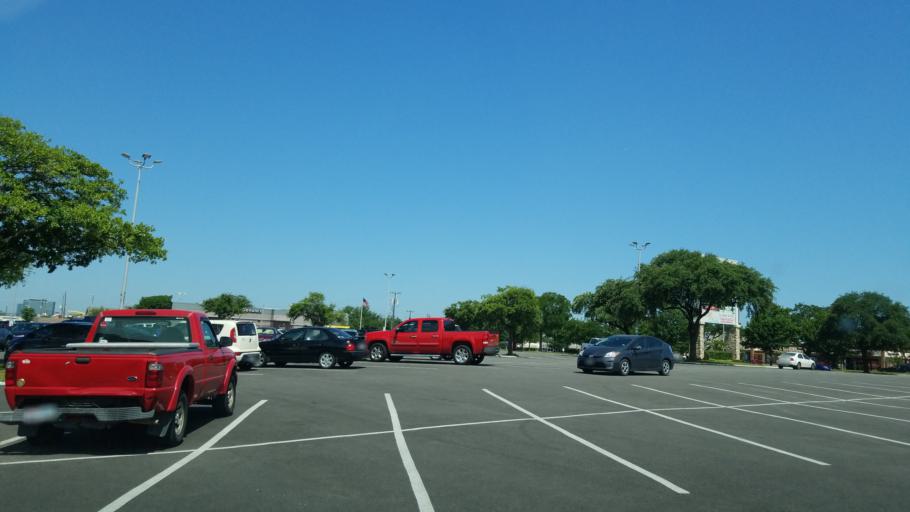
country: US
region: Texas
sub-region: Dallas County
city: Farmers Branch
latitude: 32.9086
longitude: -96.8529
